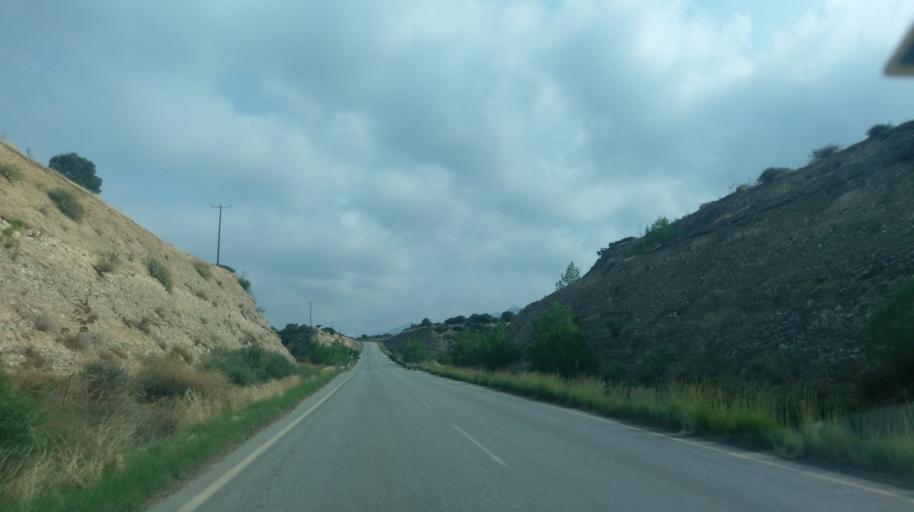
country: CY
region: Ammochostos
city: Lefkonoiko
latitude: 35.3537
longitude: 33.6456
